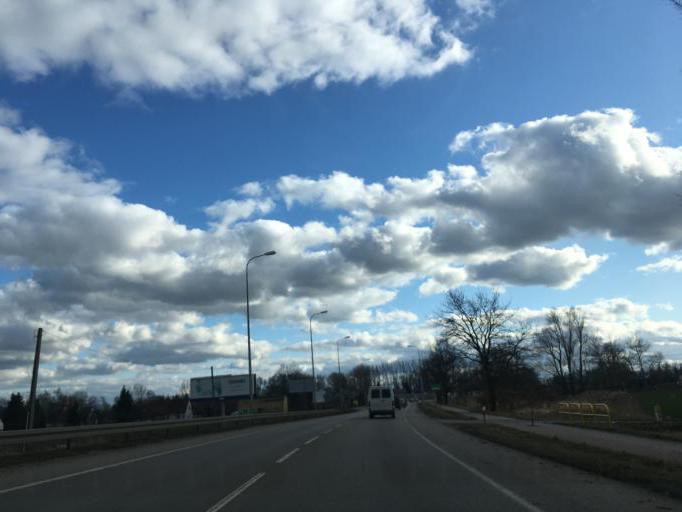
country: PL
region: Pomeranian Voivodeship
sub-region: Gdansk
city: Gdansk
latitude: 54.3336
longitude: 18.7432
